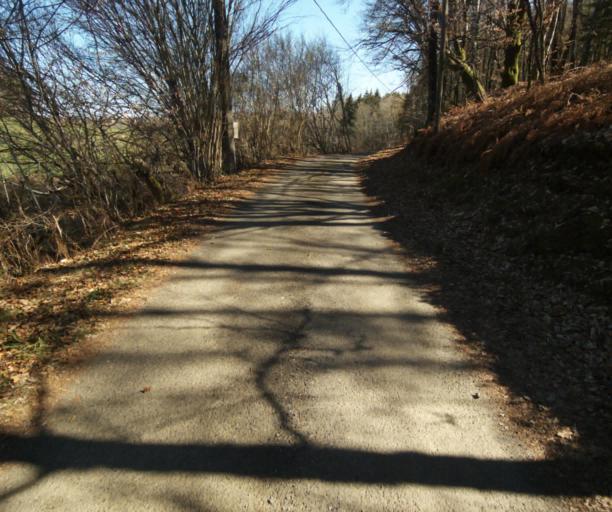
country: FR
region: Limousin
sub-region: Departement de la Correze
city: Chamboulive
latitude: 45.4052
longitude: 1.7338
